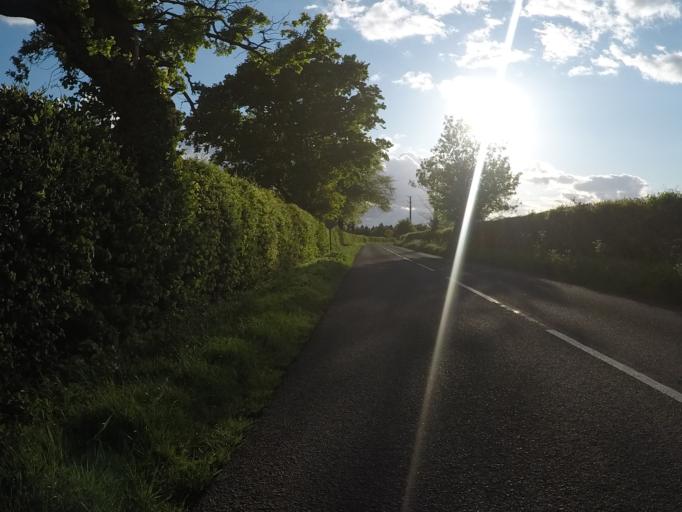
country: GB
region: England
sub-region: Oxfordshire
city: Charlbury
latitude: 51.8674
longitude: -1.4600
